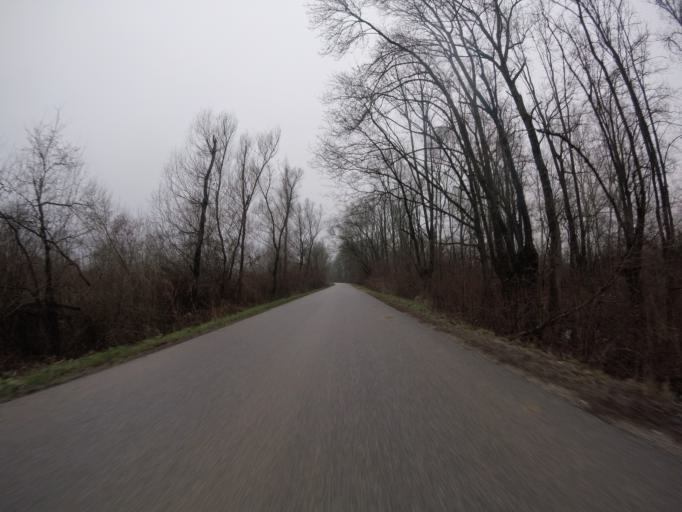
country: HR
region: Sisacko-Moslavacka
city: Lekenik
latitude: 45.6267
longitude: 16.3176
